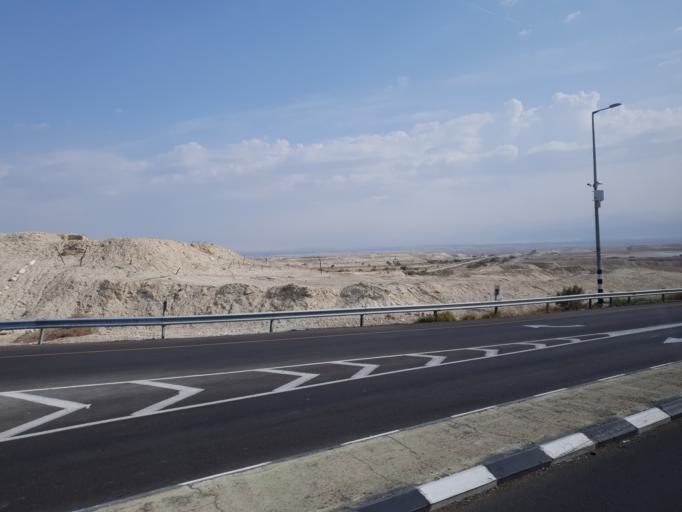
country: PS
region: West Bank
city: Jericho
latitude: 31.7993
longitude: 35.4905
